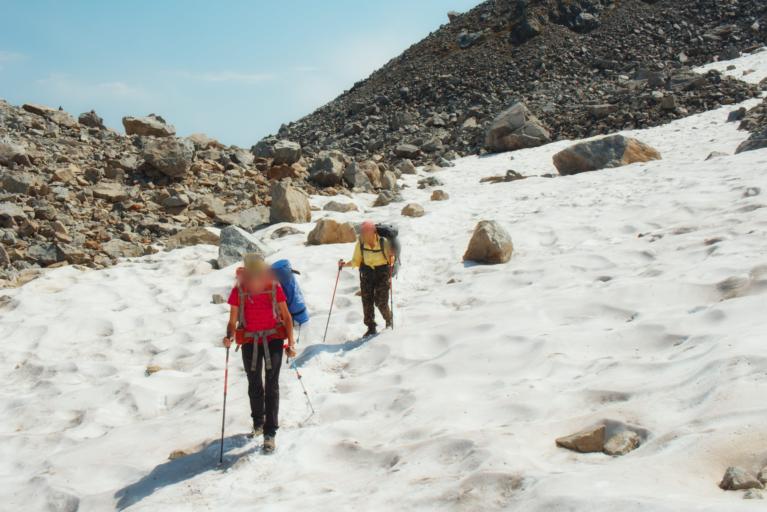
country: RU
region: Karachayevo-Cherkesiya
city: Nizhniy Arkhyz
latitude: 43.4569
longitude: 41.2227
